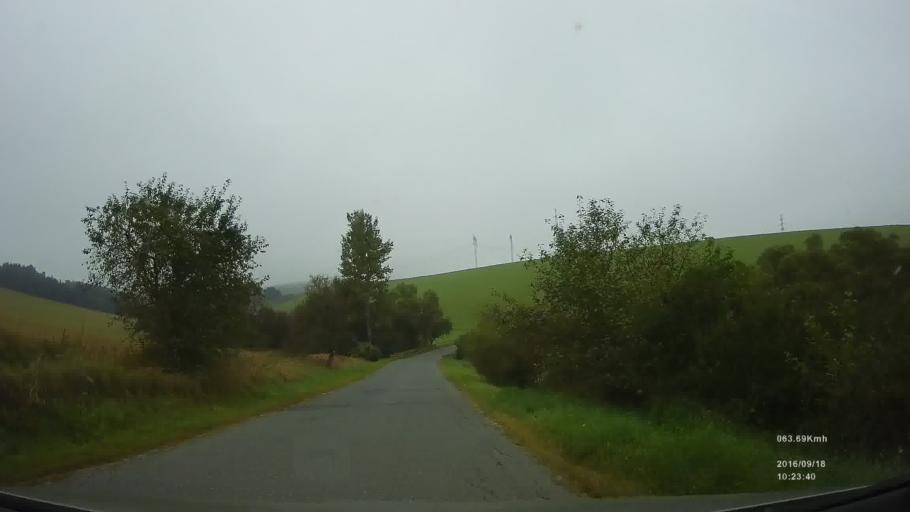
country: SK
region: Kosicky
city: Spisska Nova Ves
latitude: 48.9422
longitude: 20.6097
